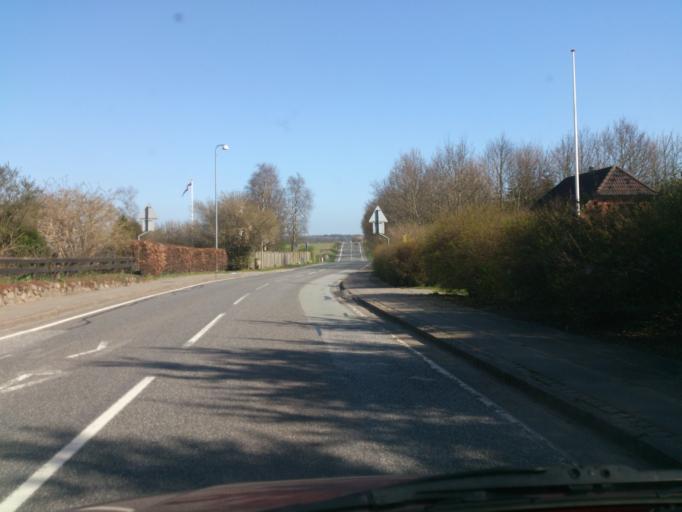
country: DK
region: Central Jutland
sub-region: Favrskov Kommune
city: Ulstrup
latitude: 56.4509
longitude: 9.7238
